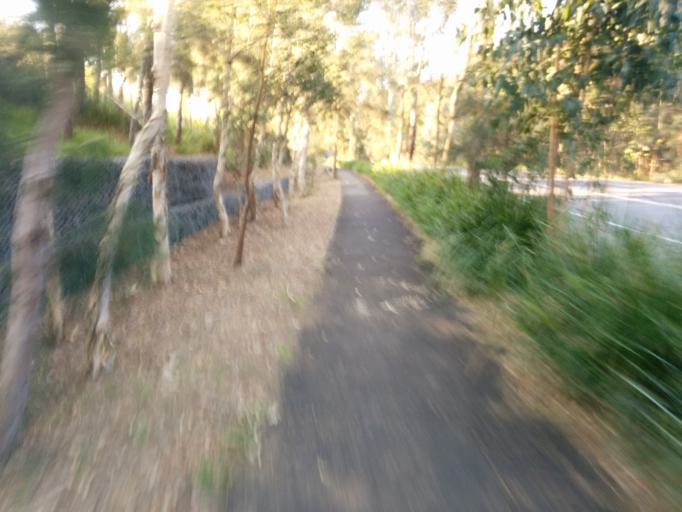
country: AU
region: New South Wales
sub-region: Canada Bay
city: Concord West
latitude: -33.8435
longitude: 151.0760
